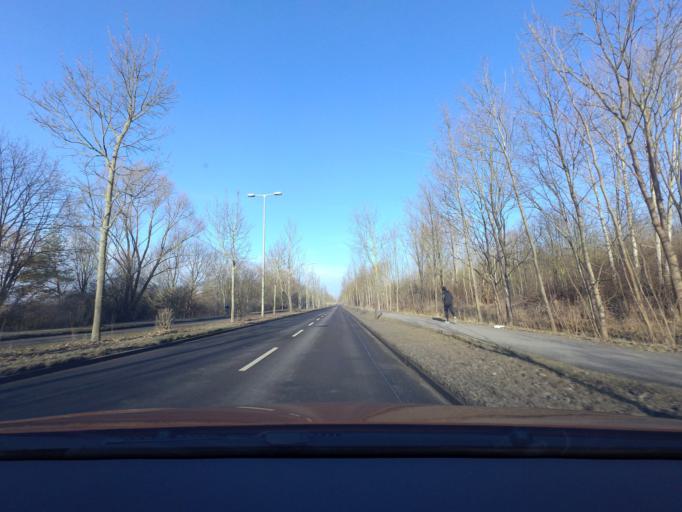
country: DE
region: Berlin
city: Blankenfelde
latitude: 52.6102
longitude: 13.3978
